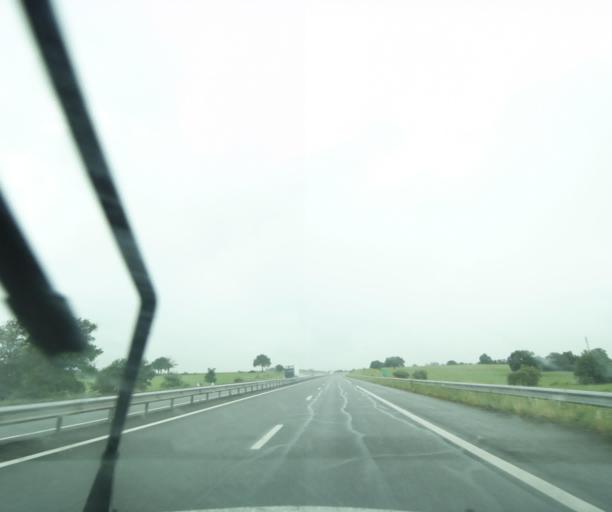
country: FR
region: Auvergne
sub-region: Departement de l'Allier
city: Vallon-en-Sully
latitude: 46.5751
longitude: 2.5314
